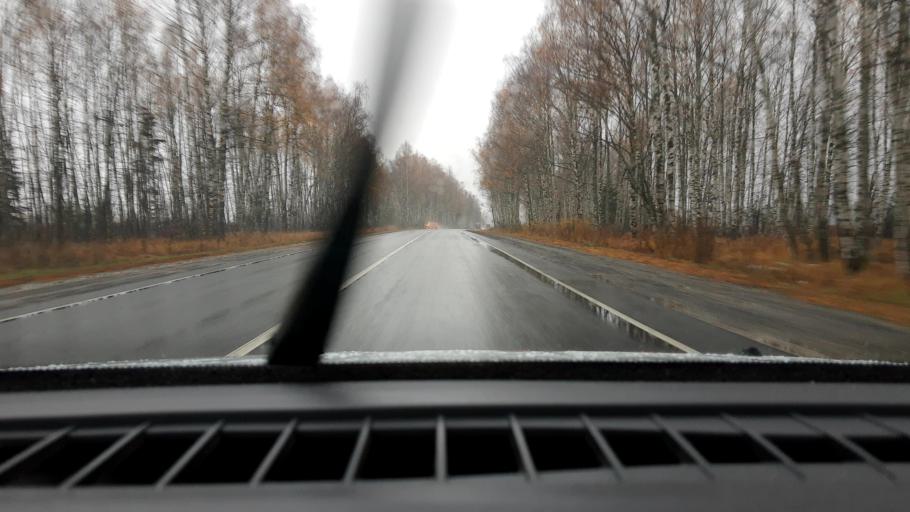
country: RU
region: Nizjnij Novgorod
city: Linda
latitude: 56.6730
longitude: 44.1429
